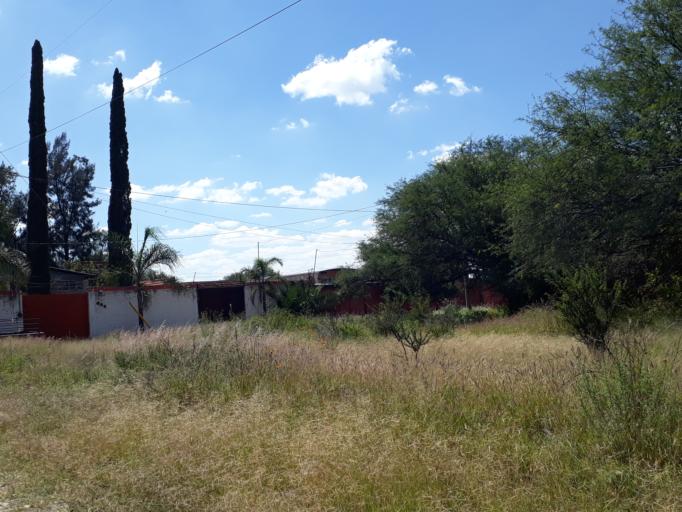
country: MX
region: Aguascalientes
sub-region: Aguascalientes
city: San Sebastian [Fraccionamiento]
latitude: 21.7862
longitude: -102.2749
